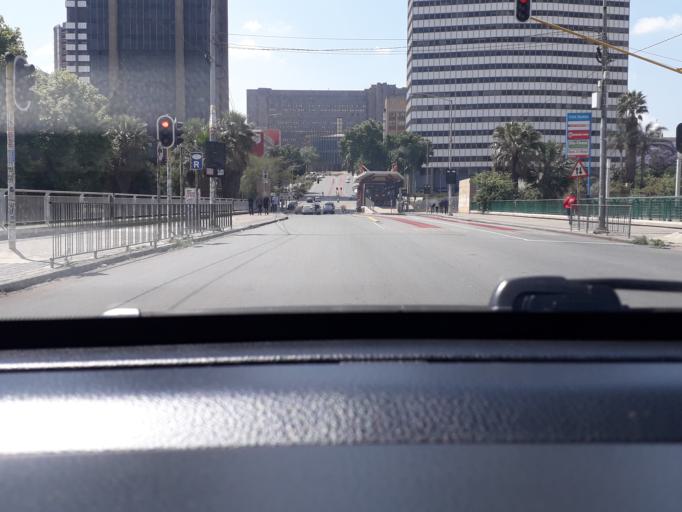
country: ZA
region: Gauteng
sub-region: City of Johannesburg Metropolitan Municipality
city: Johannesburg
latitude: -26.1967
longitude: 28.0410
